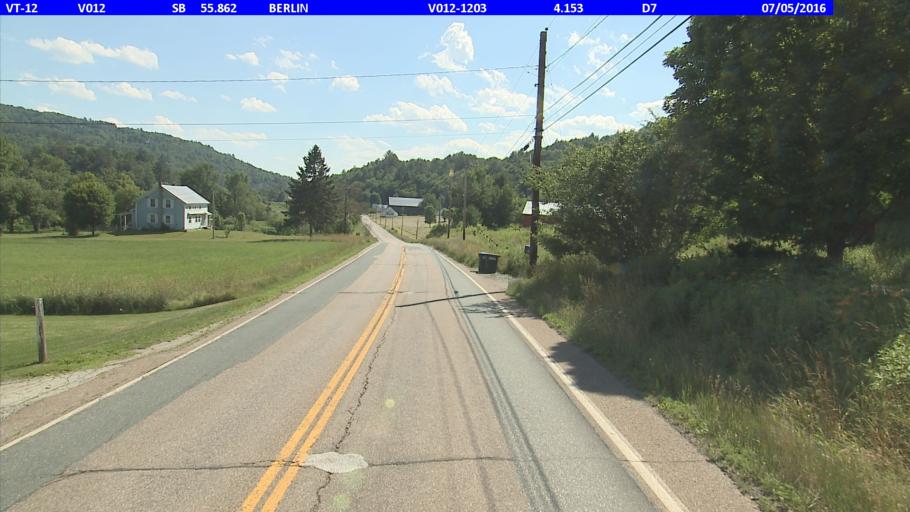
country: US
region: Vermont
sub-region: Washington County
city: Montpelier
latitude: 44.2259
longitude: -72.6210
